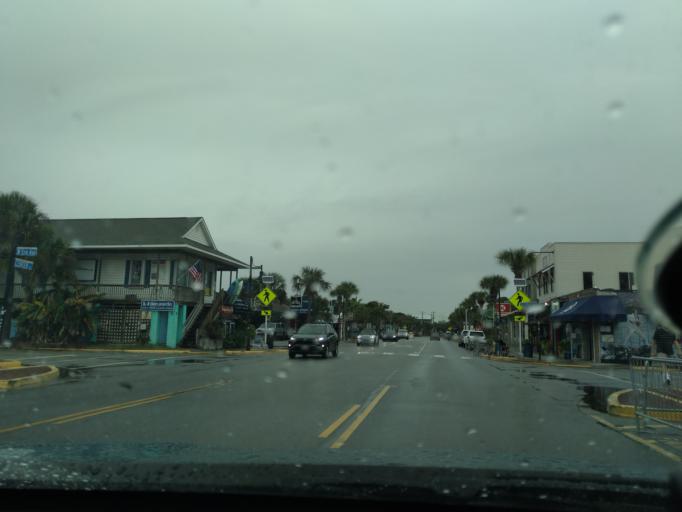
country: US
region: South Carolina
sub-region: Charleston County
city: Folly Beach
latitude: 32.6563
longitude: -79.9412
